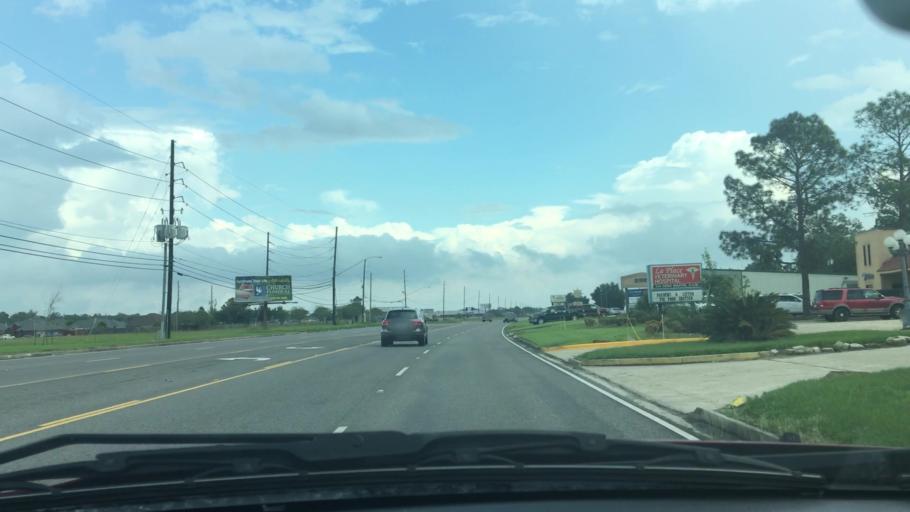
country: US
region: Louisiana
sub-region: Saint John the Baptist Parish
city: Laplace
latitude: 30.0743
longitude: -90.4735
